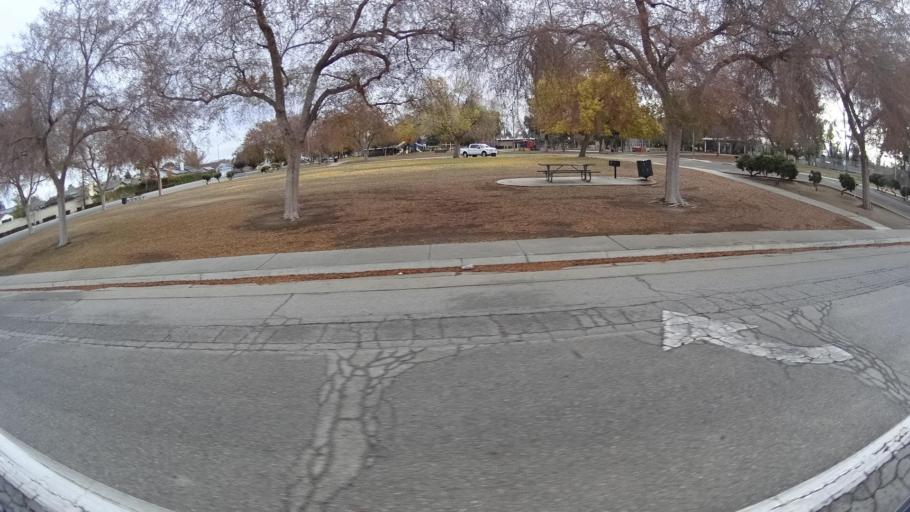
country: US
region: California
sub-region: Kern County
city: Greenacres
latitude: 35.4191
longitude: -119.0745
